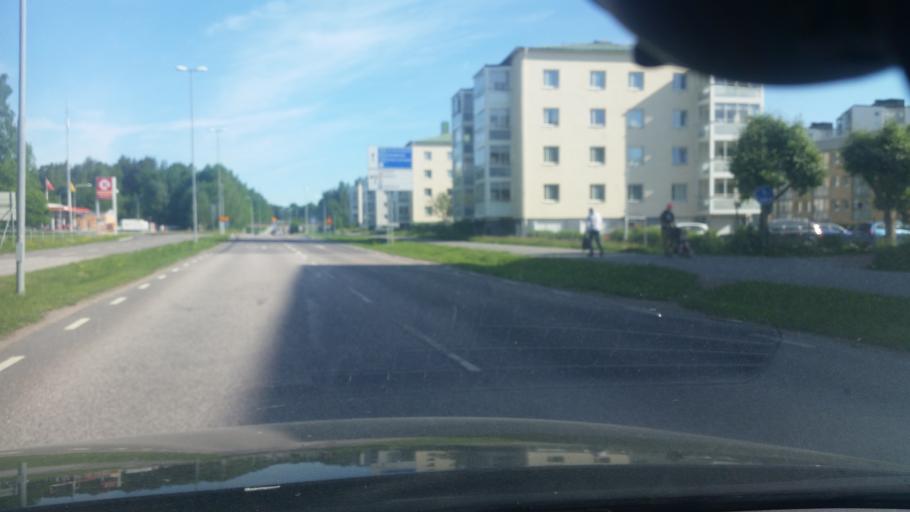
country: SE
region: Soedermanland
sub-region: Nykopings Kommun
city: Nykoping
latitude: 58.7564
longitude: 17.0346
